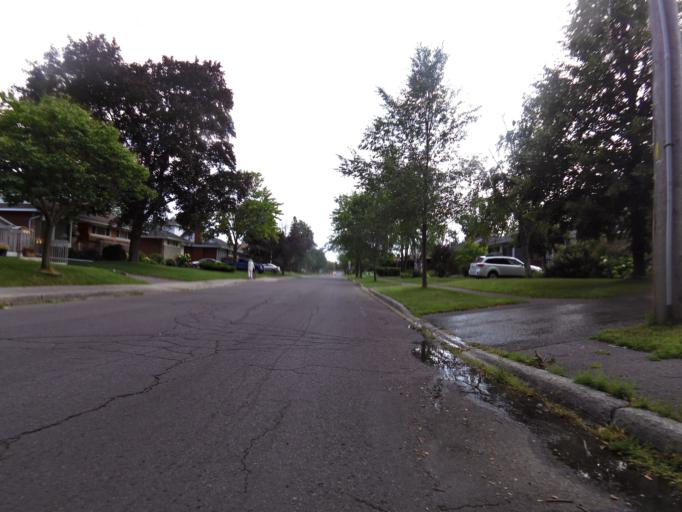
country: CA
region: Ontario
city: Ottawa
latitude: 45.3940
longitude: -75.6313
